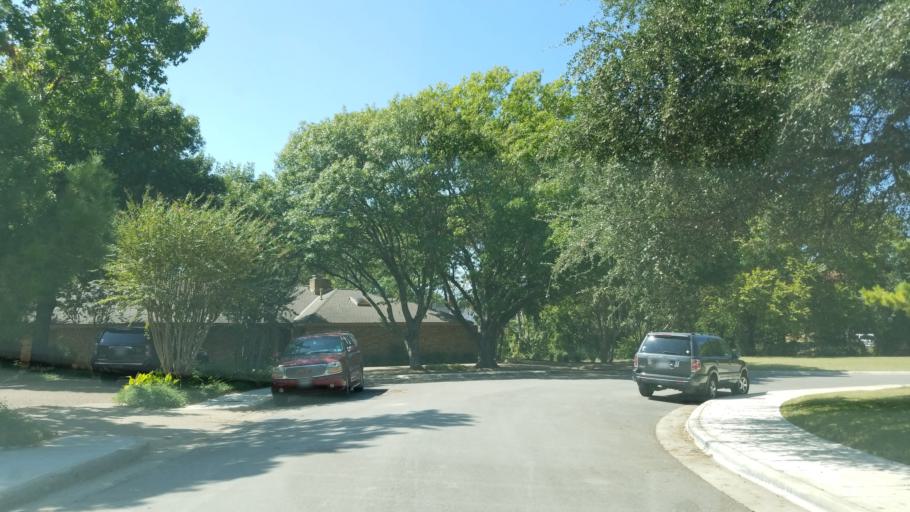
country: US
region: Texas
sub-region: Dallas County
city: Addison
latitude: 32.9702
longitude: -96.7917
